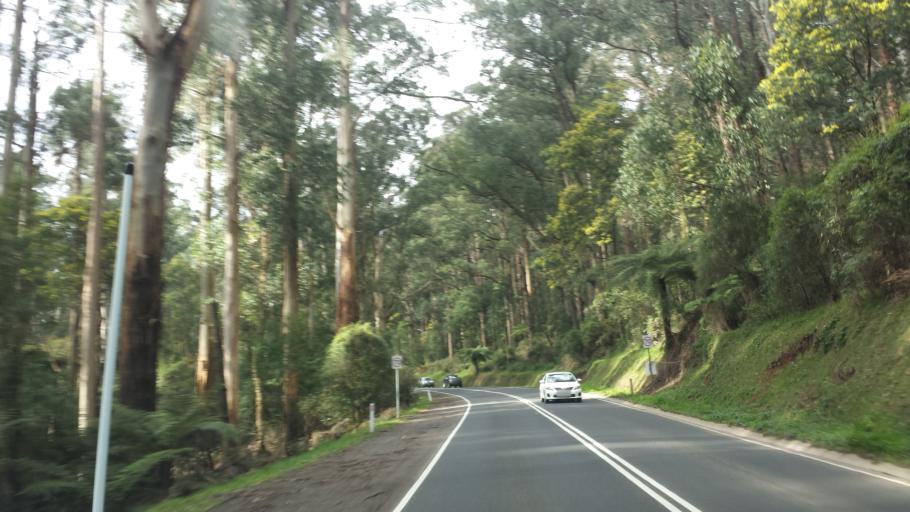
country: AU
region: Victoria
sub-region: Yarra Ranges
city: Belgrave
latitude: -37.8963
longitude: 145.3602
